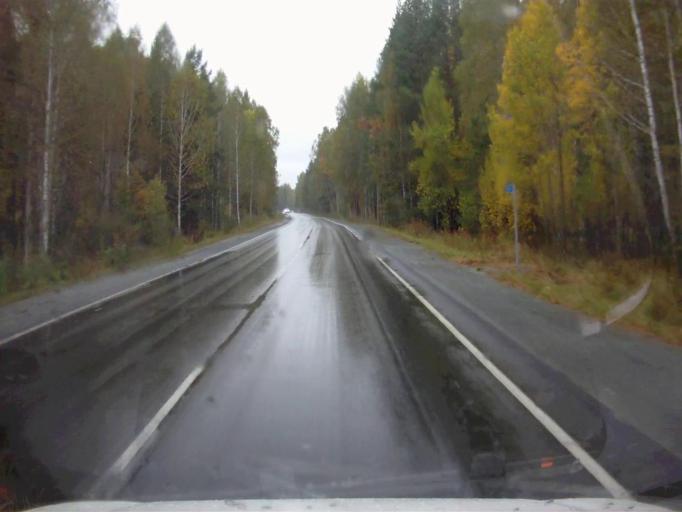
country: RU
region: Chelyabinsk
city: Tayginka
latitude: 55.5931
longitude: 60.6245
